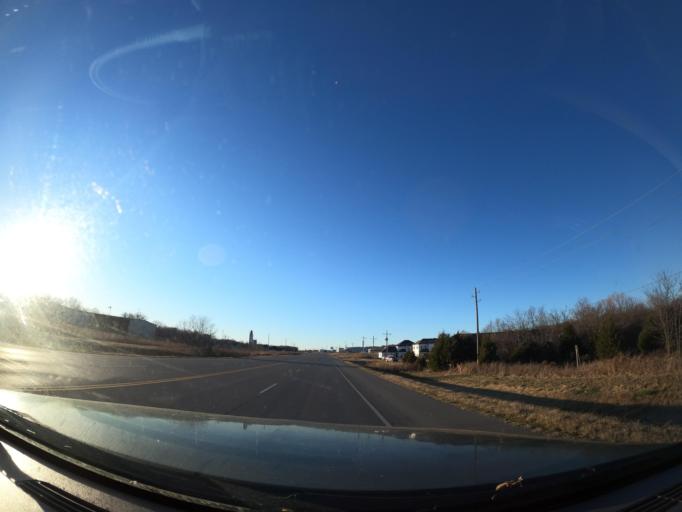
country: US
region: Oklahoma
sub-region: Pittsburg County
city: Krebs
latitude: 34.8958
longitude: -95.6711
